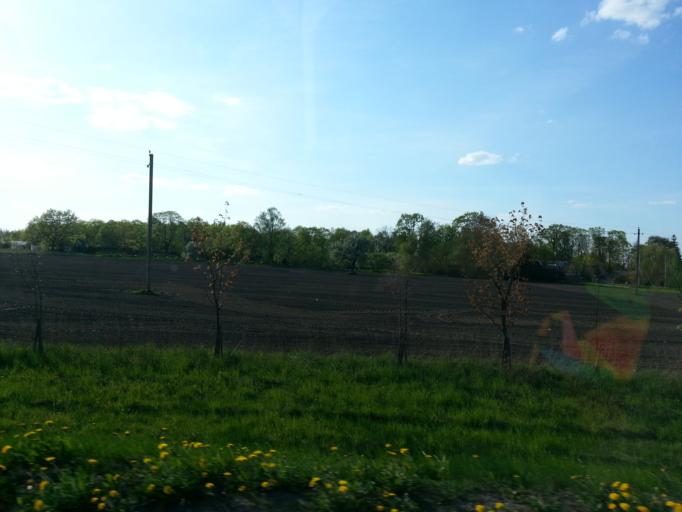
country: LT
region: Panevezys
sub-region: Panevezys City
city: Panevezys
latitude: 55.7957
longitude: 24.3178
